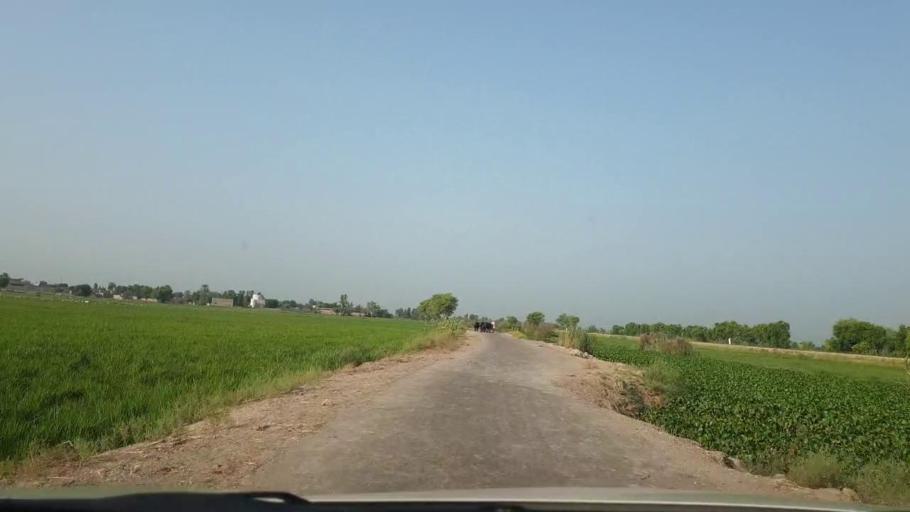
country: PK
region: Sindh
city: Larkana
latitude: 27.5094
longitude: 68.1826
